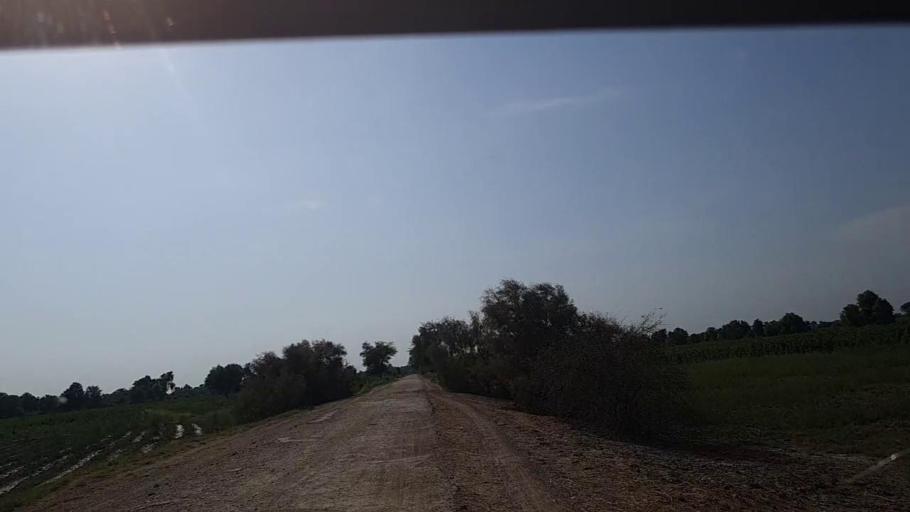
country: PK
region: Sindh
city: Adilpur
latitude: 27.8397
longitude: 69.3143
